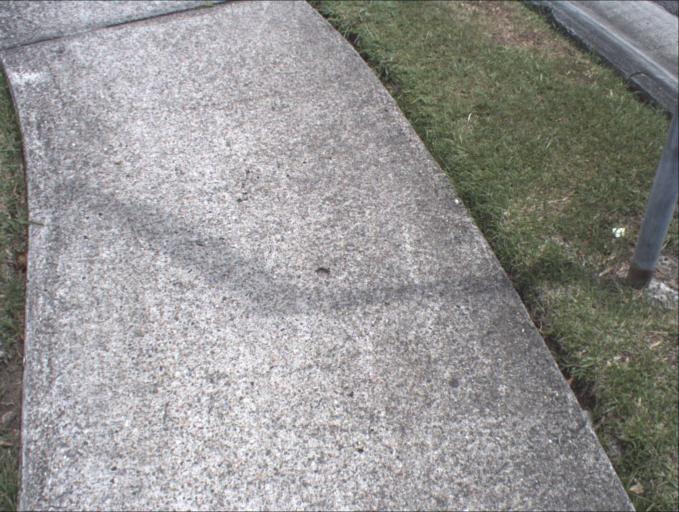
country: AU
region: Queensland
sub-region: Logan
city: Slacks Creek
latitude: -27.6706
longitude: 153.1472
